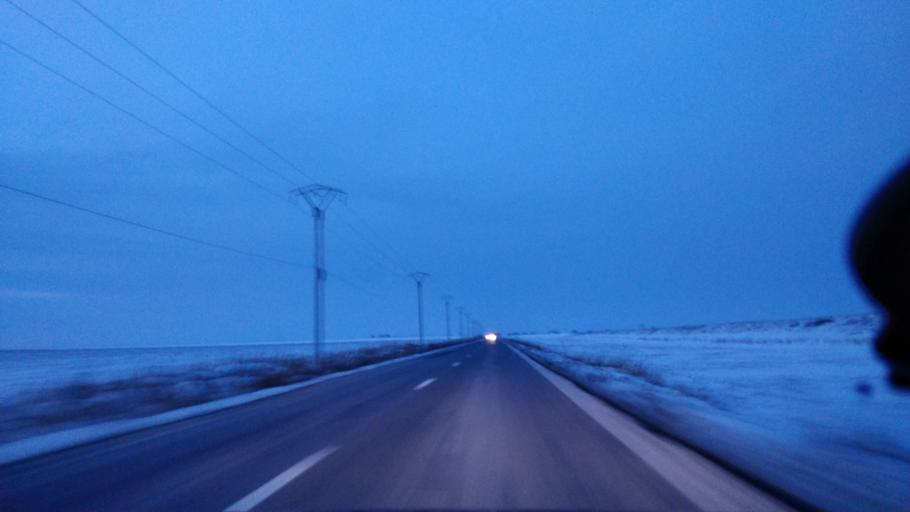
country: RO
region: Vrancea
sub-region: Comuna Nanesti
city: Nanesti
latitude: 45.5670
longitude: 27.4990
